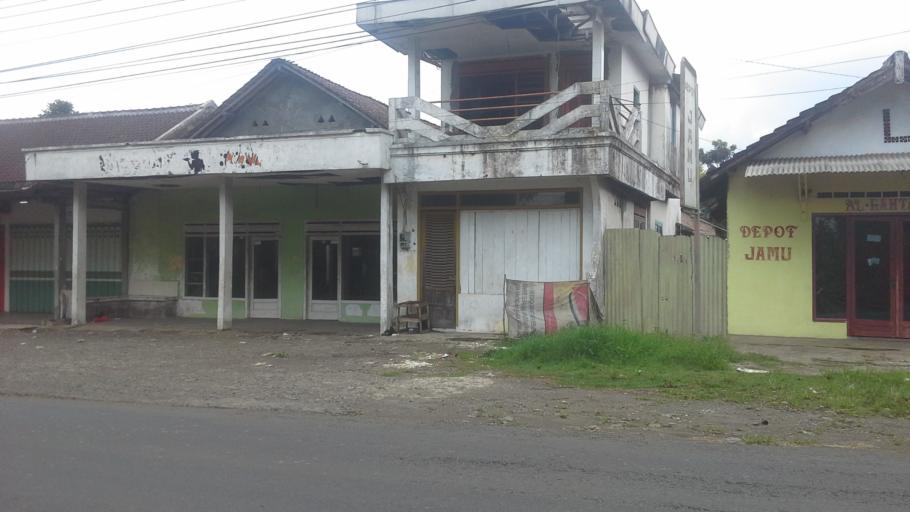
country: ID
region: East Java
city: Krajan Satu Pekauman
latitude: -7.9800
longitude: 113.7953
